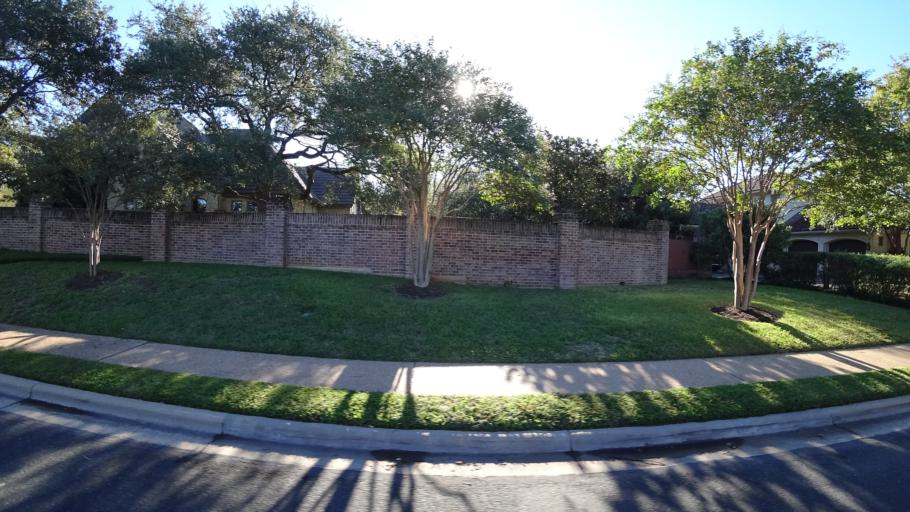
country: US
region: Texas
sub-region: Travis County
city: West Lake Hills
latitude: 30.3352
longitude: -97.8039
